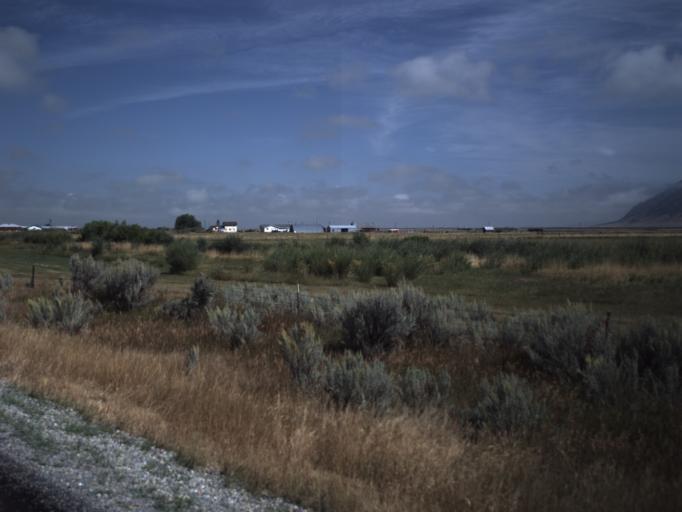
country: US
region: Utah
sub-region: Rich County
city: Randolph
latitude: 41.5929
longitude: -111.1724
